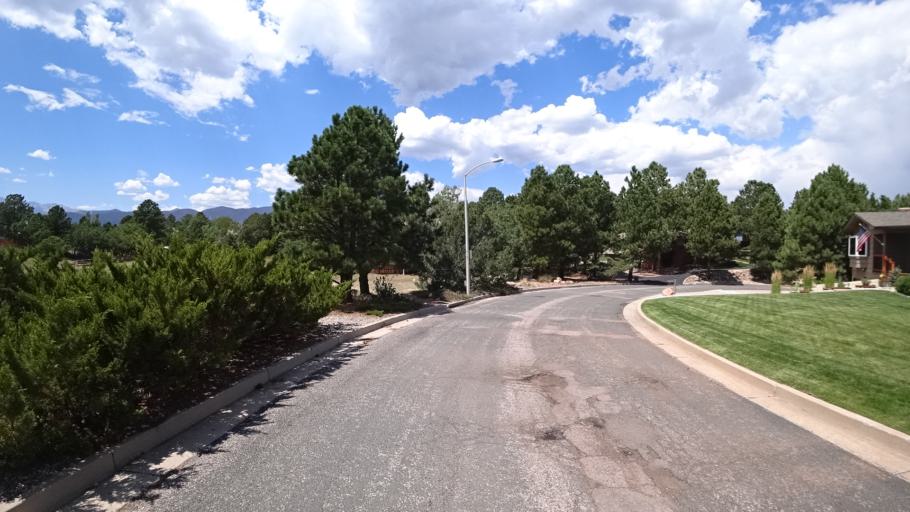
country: US
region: Colorado
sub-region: El Paso County
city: Air Force Academy
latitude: 38.9329
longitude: -104.8254
